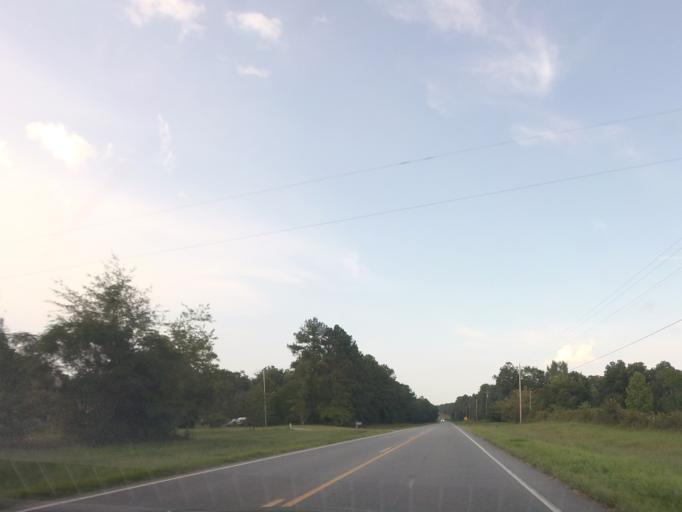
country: US
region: Georgia
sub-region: Bleckley County
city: Cochran
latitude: 32.4285
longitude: -83.3084
